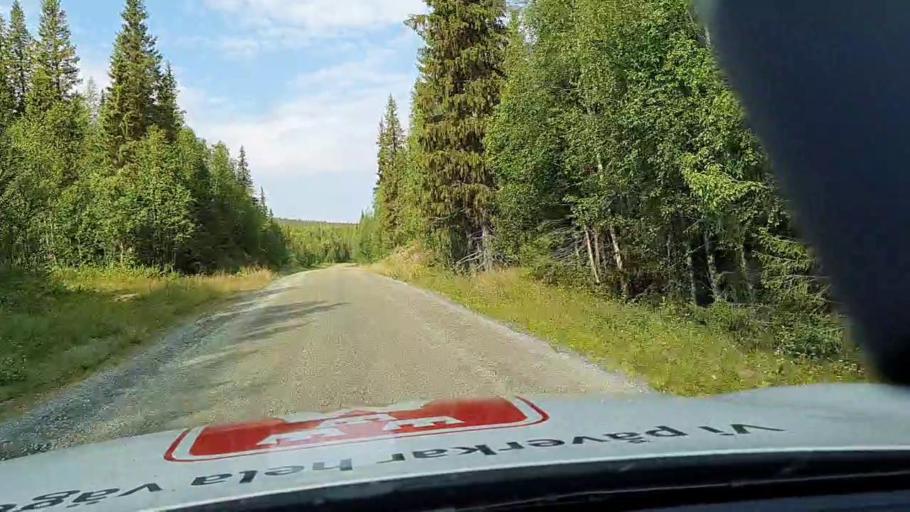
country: SE
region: Vaesterbotten
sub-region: Storumans Kommun
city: Fristad
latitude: 65.5386
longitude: 16.8059
